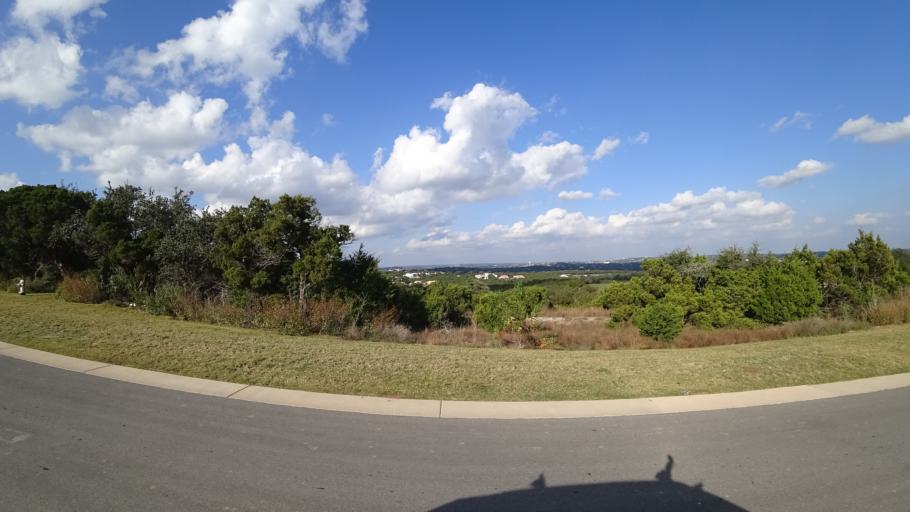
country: US
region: Texas
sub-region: Travis County
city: Barton Creek
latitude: 30.2625
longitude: -97.8810
